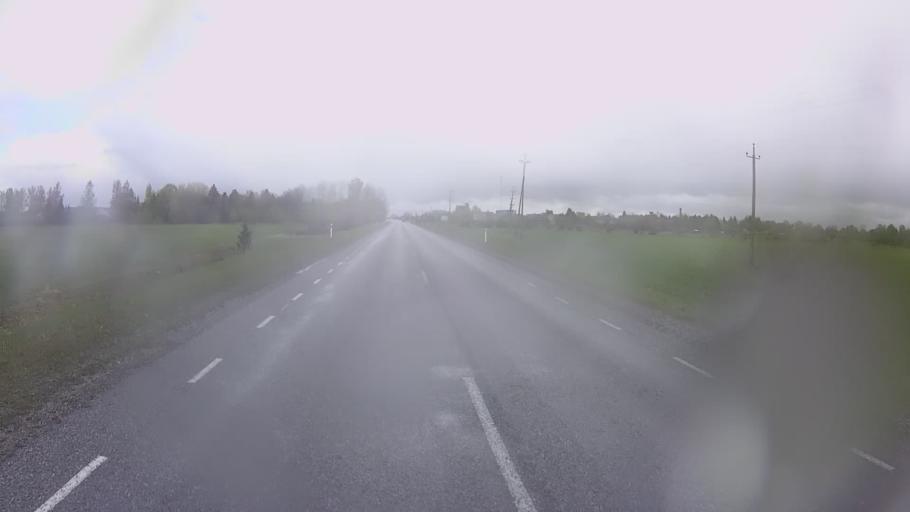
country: EE
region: Hiiumaa
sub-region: Kaerdla linn
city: Kardla
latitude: 58.8288
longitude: 22.7627
